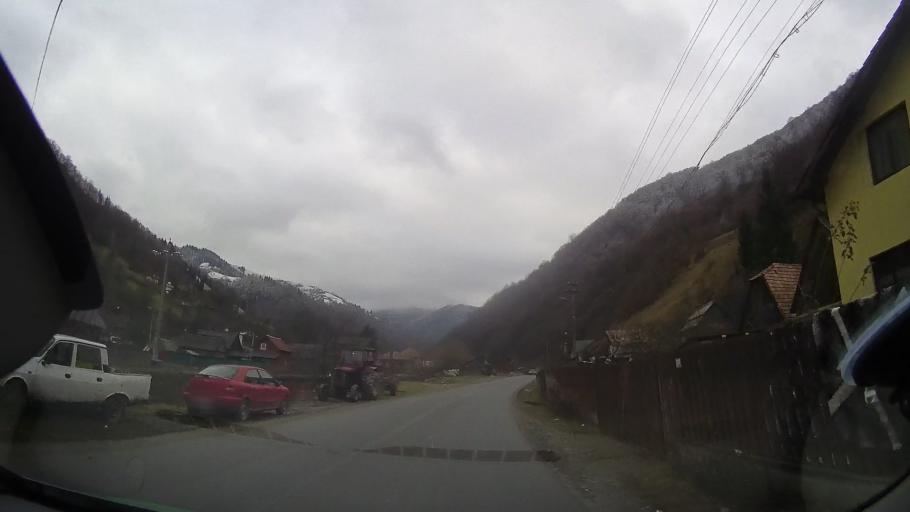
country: RO
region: Cluj
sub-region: Comuna Maguri-Racatau
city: Maguri-Racatau
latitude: 46.6463
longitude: 23.1956
